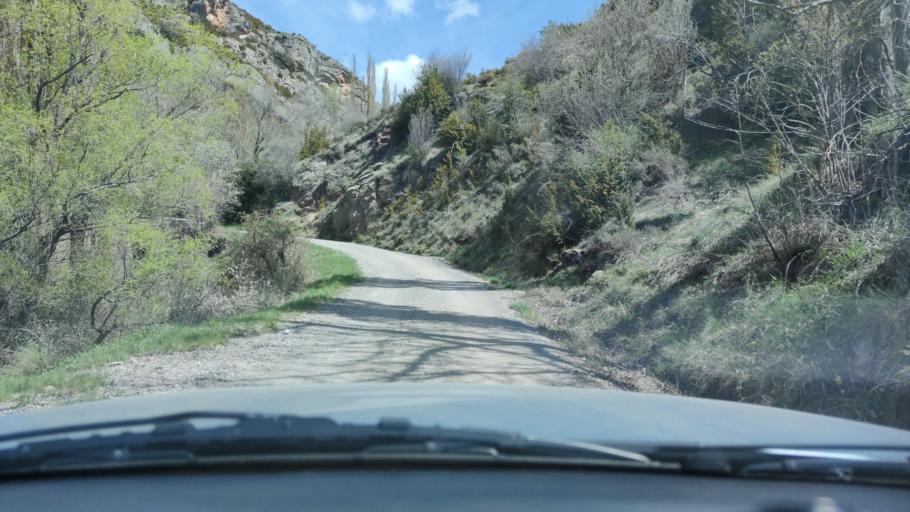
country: ES
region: Catalonia
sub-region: Provincia de Lleida
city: Sort
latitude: 42.2994
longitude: 1.1795
